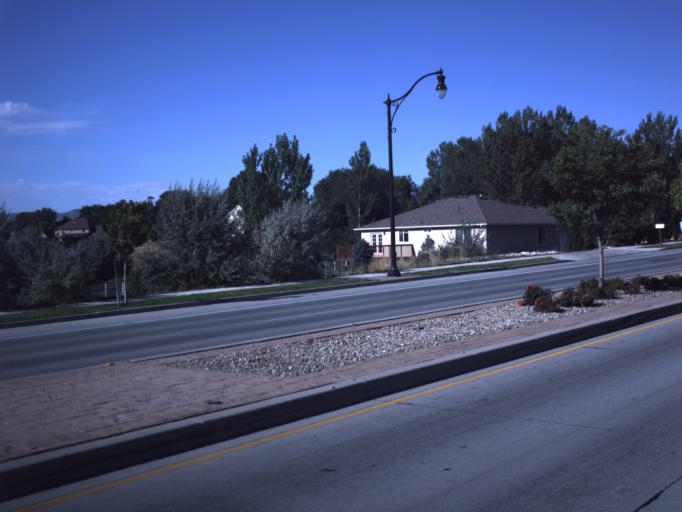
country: US
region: Utah
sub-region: Salt Lake County
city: South Jordan
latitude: 40.5441
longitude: -111.9070
